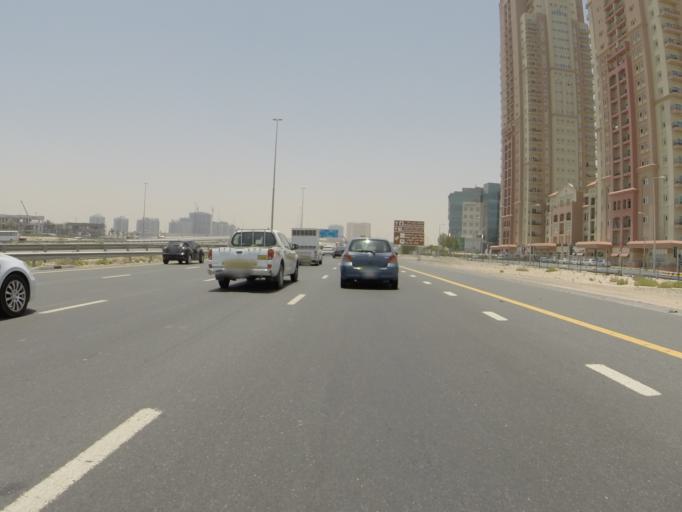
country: AE
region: Dubai
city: Dubai
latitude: 25.0495
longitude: 55.1957
